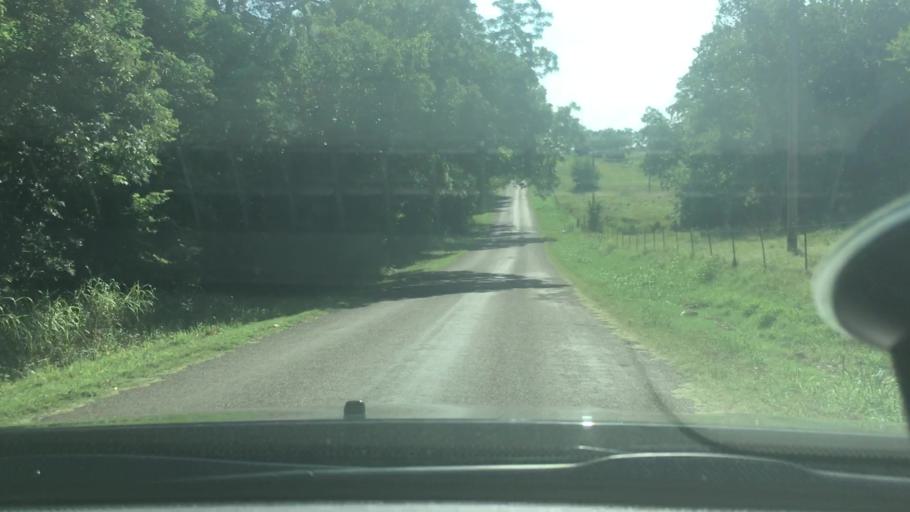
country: US
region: Oklahoma
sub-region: Garvin County
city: Pauls Valley
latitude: 34.6521
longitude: -97.3570
